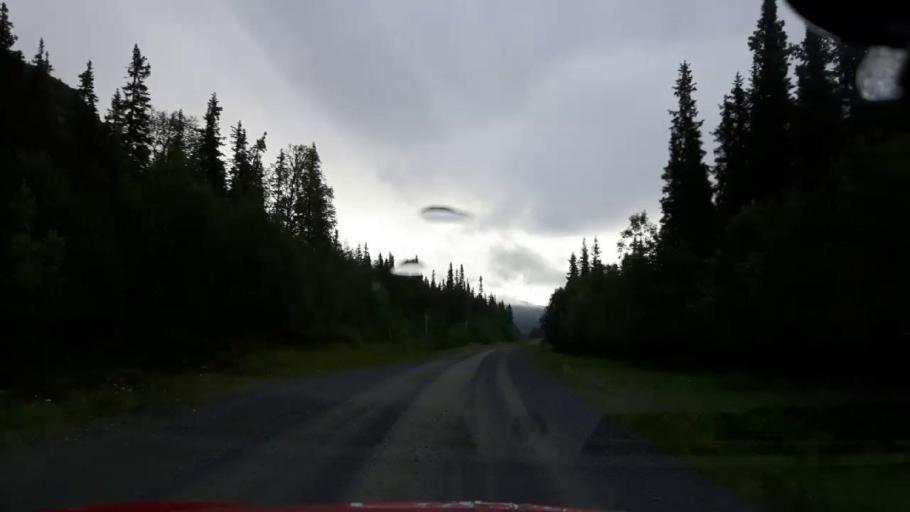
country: NO
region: Nordland
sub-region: Hattfjelldal
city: Hattfjelldal
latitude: 64.8828
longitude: 14.7779
